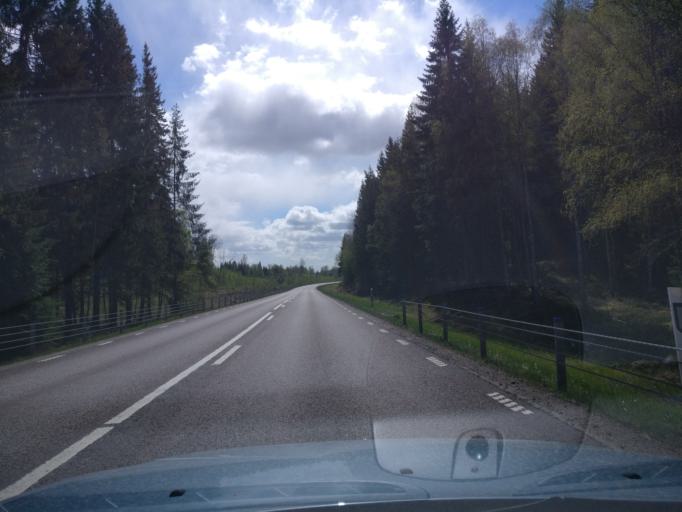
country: SE
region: Vaermland
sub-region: Karlstads Kommun
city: Molkom
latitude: 59.5655
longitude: 13.6666
